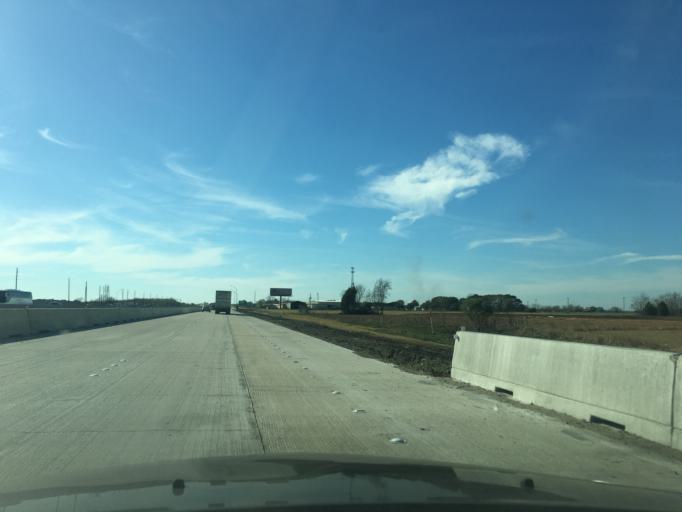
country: US
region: Texas
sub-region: Fort Bend County
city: Pleak
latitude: 29.4893
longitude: -95.9243
